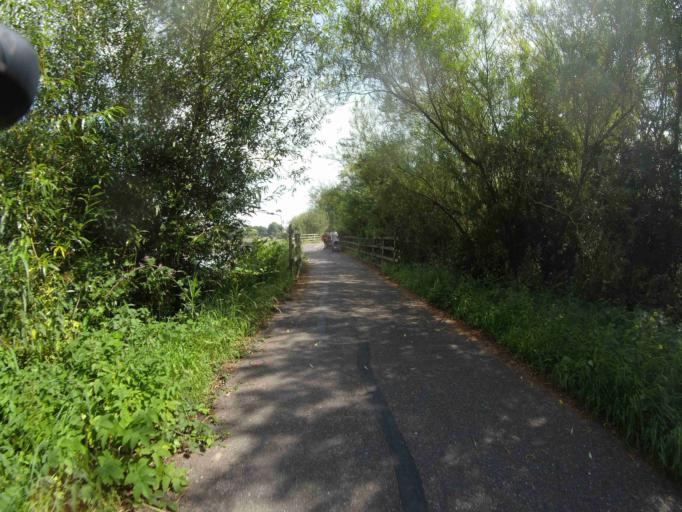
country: GB
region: England
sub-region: Devon
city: Exminster
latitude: 50.6939
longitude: -3.4984
